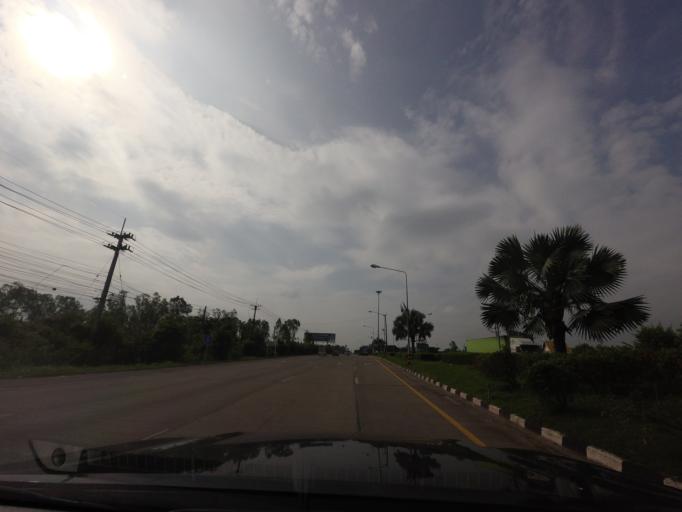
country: TH
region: Nong Khai
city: Nong Khai
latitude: 17.8140
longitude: 102.7589
